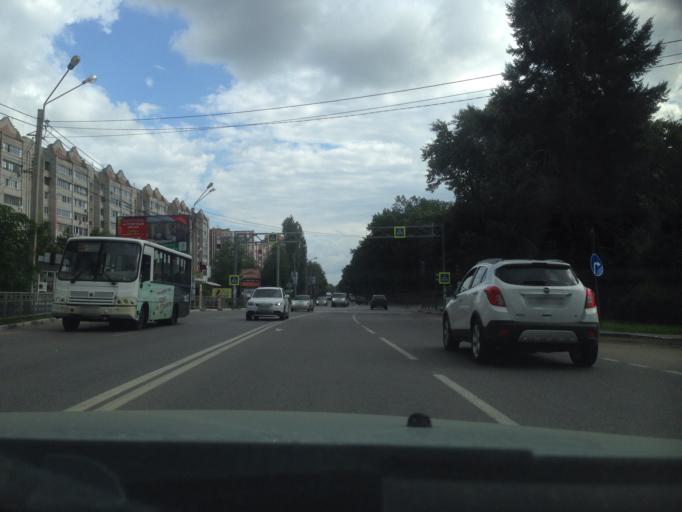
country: RU
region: Voronezj
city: Podgornoye
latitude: 51.7260
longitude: 39.2003
